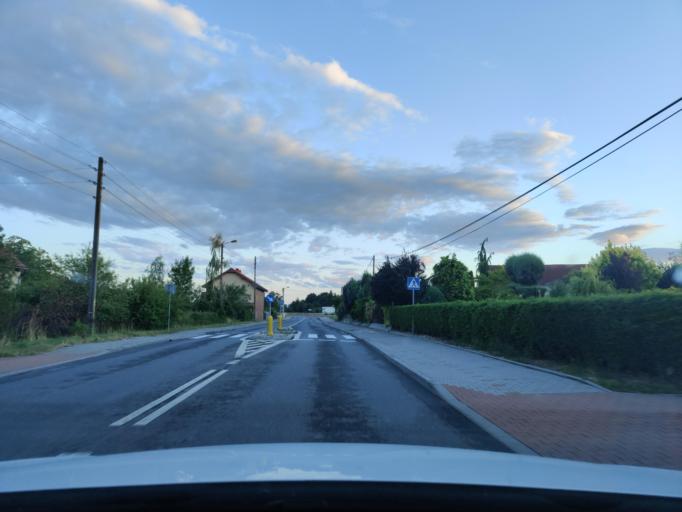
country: PL
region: Opole Voivodeship
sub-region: Powiat nyski
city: Chroscina
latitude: 50.6497
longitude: 17.3842
